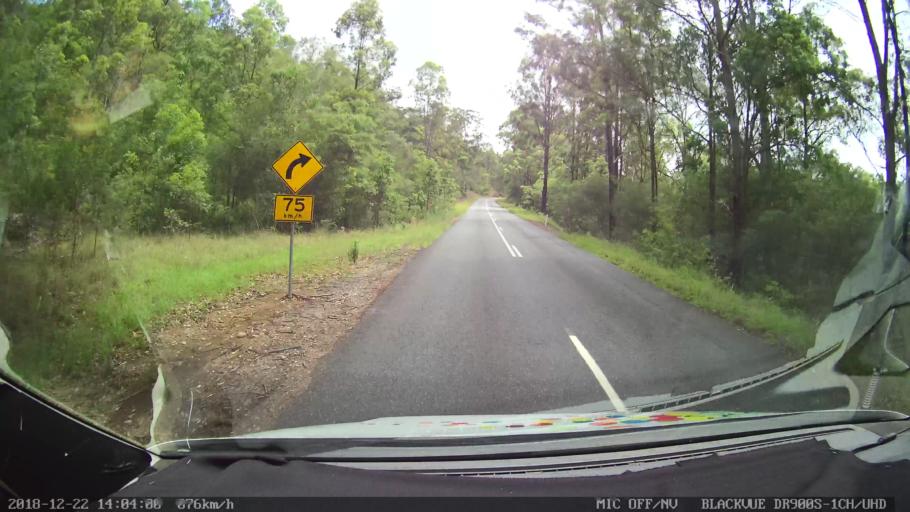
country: AU
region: New South Wales
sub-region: Clarence Valley
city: Coutts Crossing
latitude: -29.9334
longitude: 152.7330
